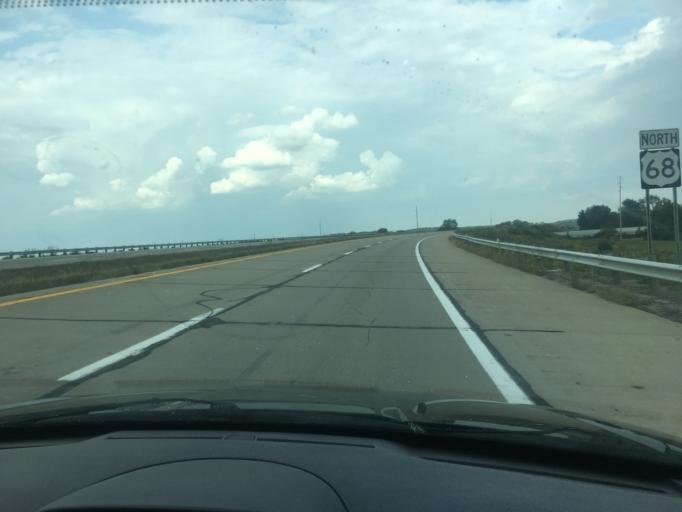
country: US
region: Ohio
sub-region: Clark County
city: Northridge
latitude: 40.0327
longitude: -83.7998
